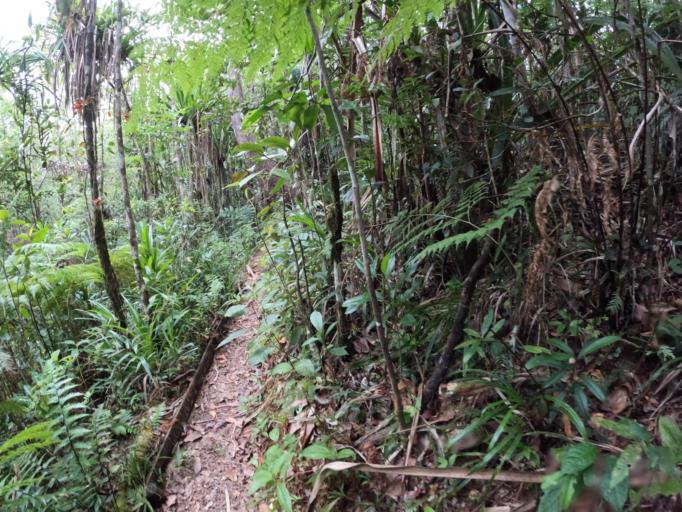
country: FJ
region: Central
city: Suva
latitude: -18.0567
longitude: 178.4633
